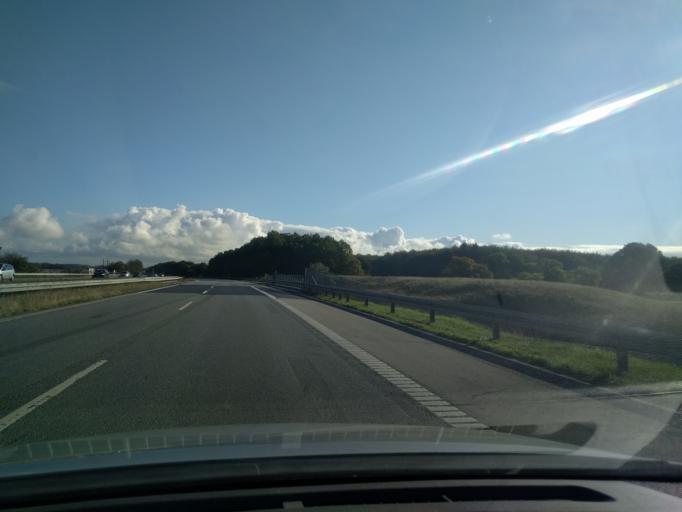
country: DK
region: Zealand
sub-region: Ringsted Kommune
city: Ringsted
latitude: 55.4555
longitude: 11.8671
